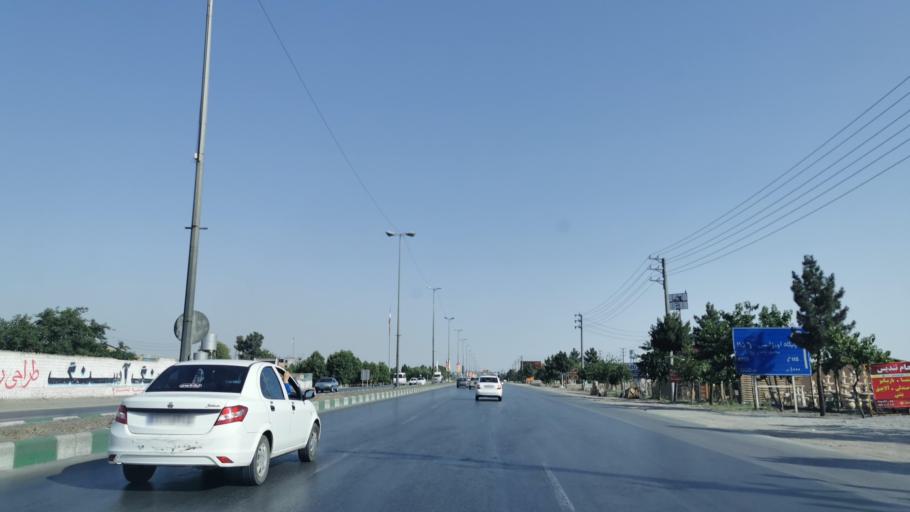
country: IR
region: Razavi Khorasan
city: Torqabeh
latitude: 36.4225
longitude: 59.4606
